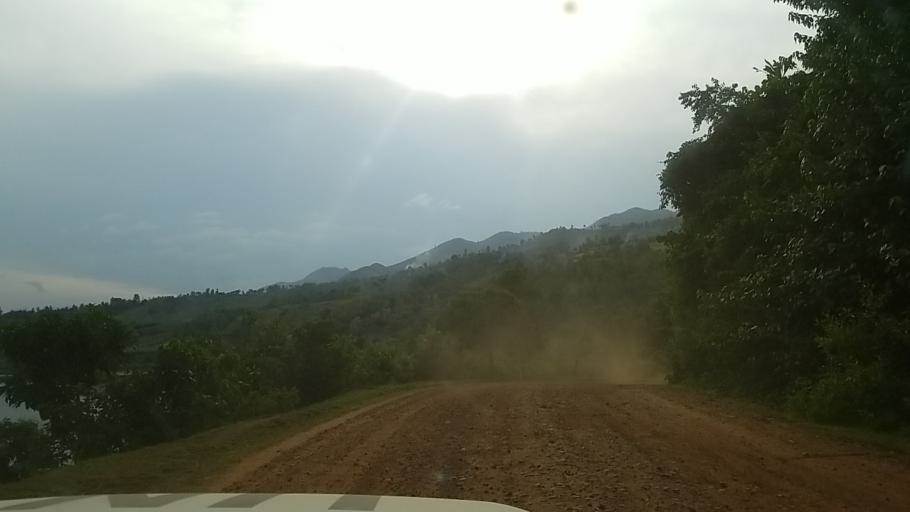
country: RW
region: Western Province
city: Cyangugu
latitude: -2.1054
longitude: 28.9113
